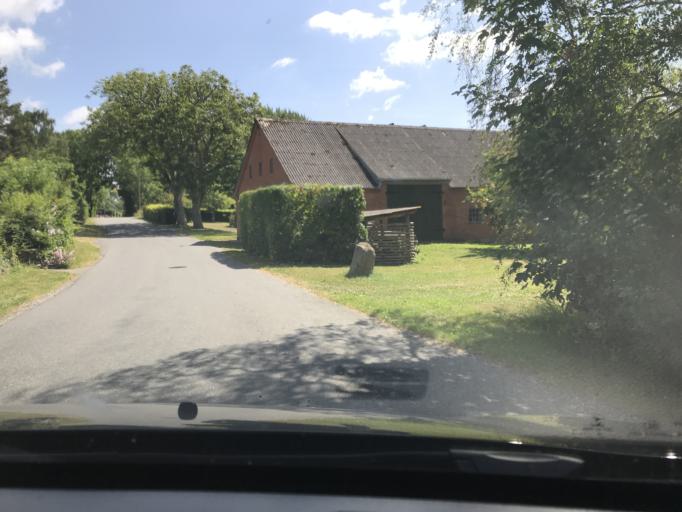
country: DK
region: South Denmark
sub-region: AEro Kommune
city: AEroskobing
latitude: 54.9118
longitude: 10.3011
